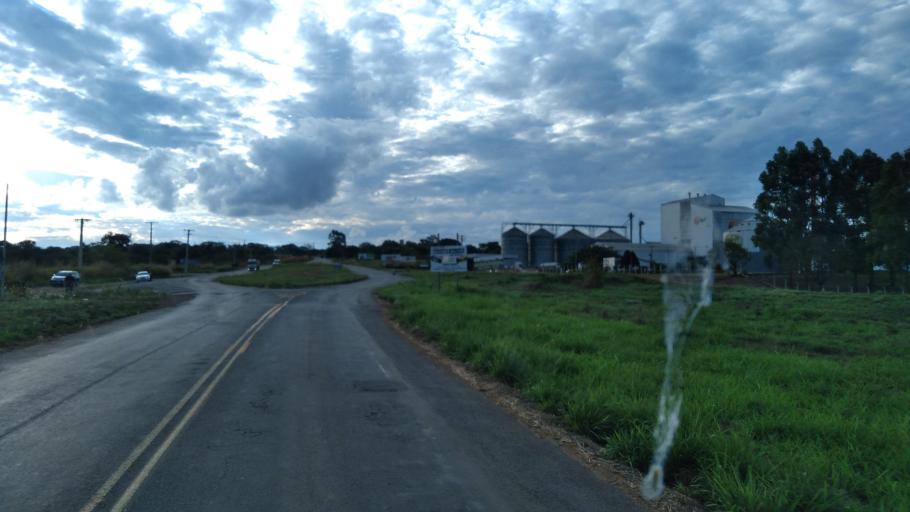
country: BR
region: Goias
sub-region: Mineiros
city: Mineiros
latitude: -17.5782
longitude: -52.5181
